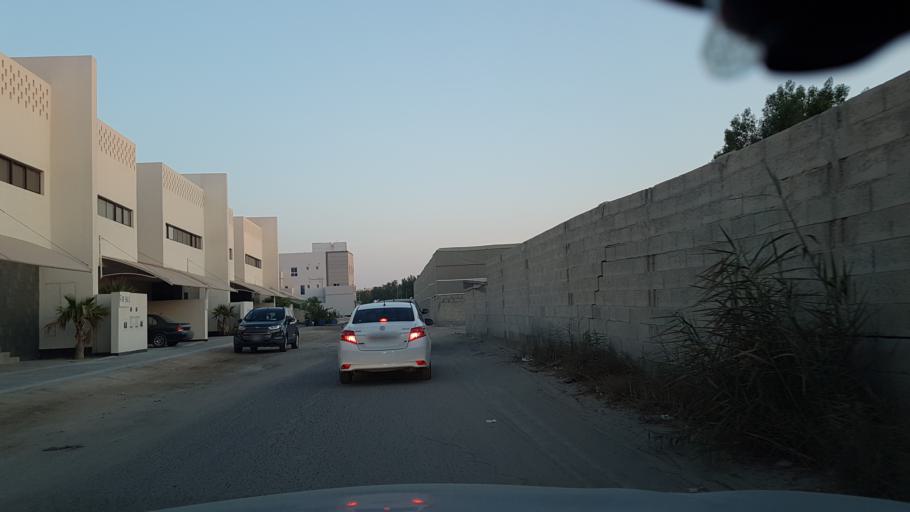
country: BH
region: Manama
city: Jidd Hafs
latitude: 26.2334
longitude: 50.5057
